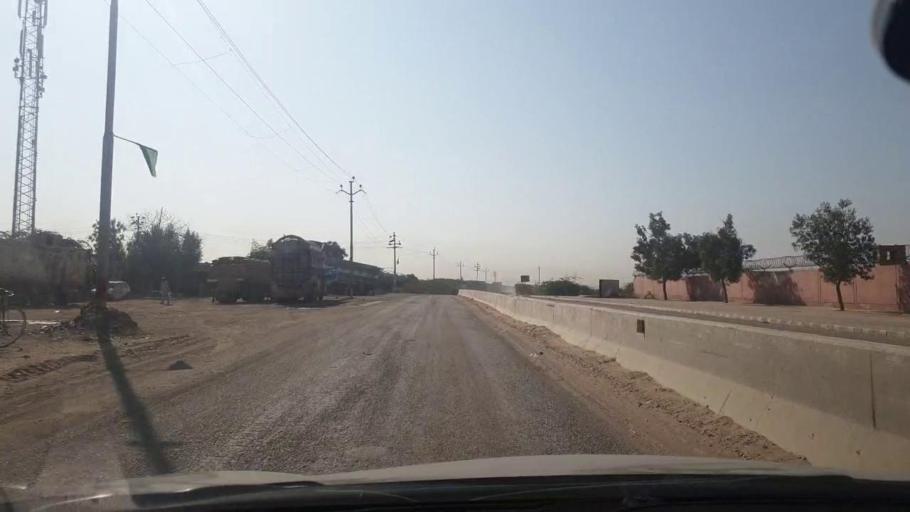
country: PK
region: Sindh
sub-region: Karachi District
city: Karachi
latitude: 25.0788
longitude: 67.0136
